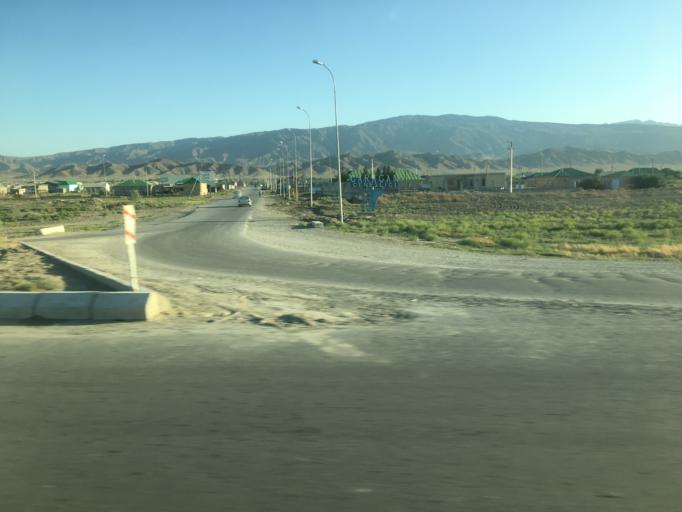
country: TM
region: Ahal
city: Baharly
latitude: 38.3808
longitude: 57.5013
